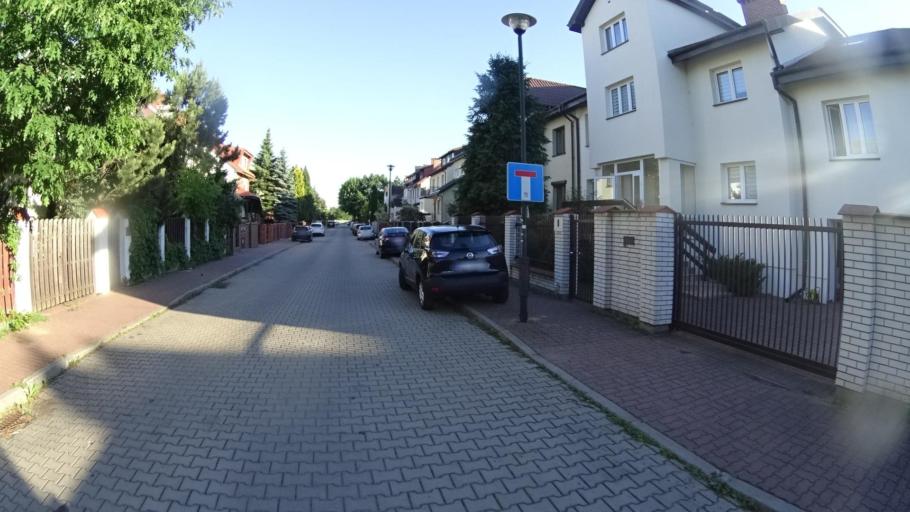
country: PL
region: Masovian Voivodeship
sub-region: Warszawa
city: Bemowo
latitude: 52.2637
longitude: 20.9132
